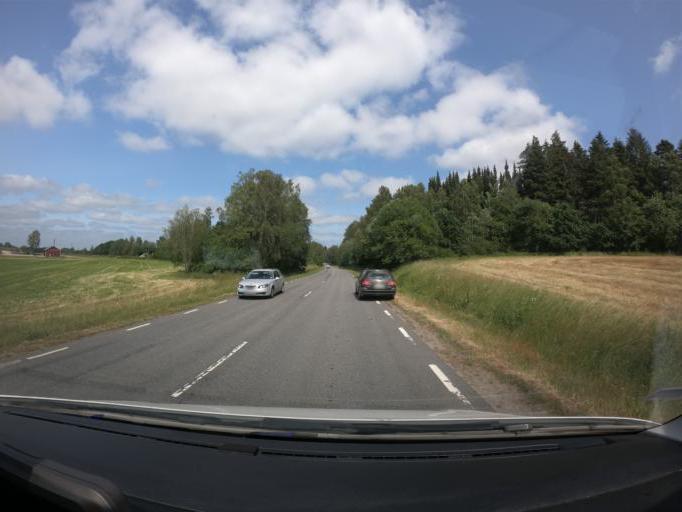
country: SE
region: Skane
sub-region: Hassleholms Kommun
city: Sosdala
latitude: 56.0456
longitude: 13.6921
